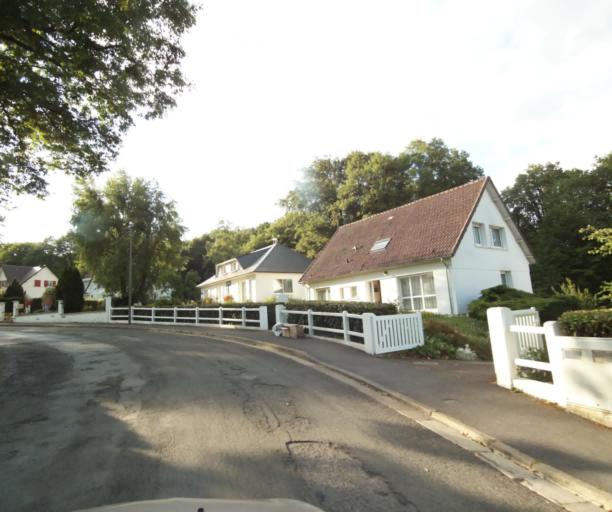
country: FR
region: Champagne-Ardenne
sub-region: Departement des Ardennes
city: Charleville-Mezieres
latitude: 49.7996
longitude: 4.7141
